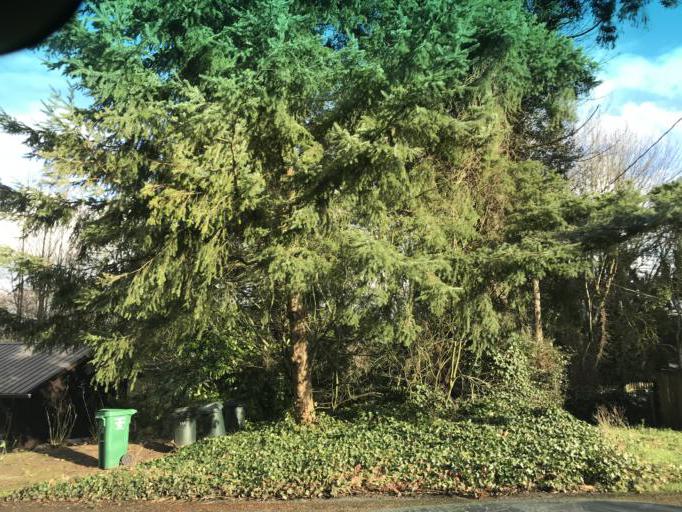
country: US
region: Washington
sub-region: King County
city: Lake Forest Park
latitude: 47.7175
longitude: -122.3046
